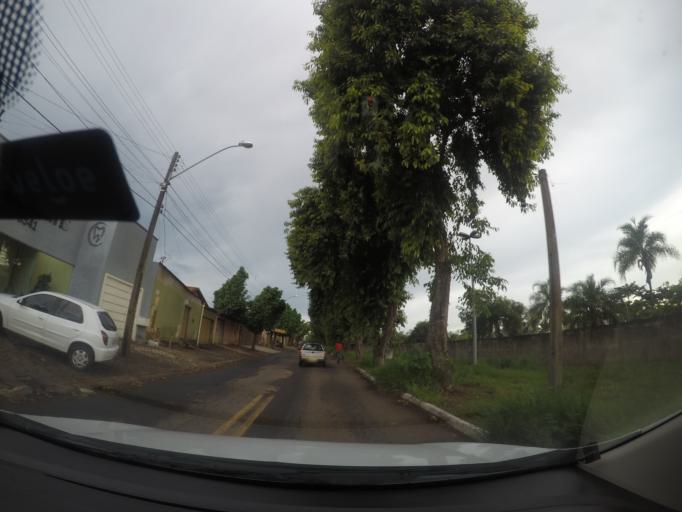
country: BR
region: Goias
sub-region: Goiania
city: Goiania
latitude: -16.7228
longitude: -49.3101
